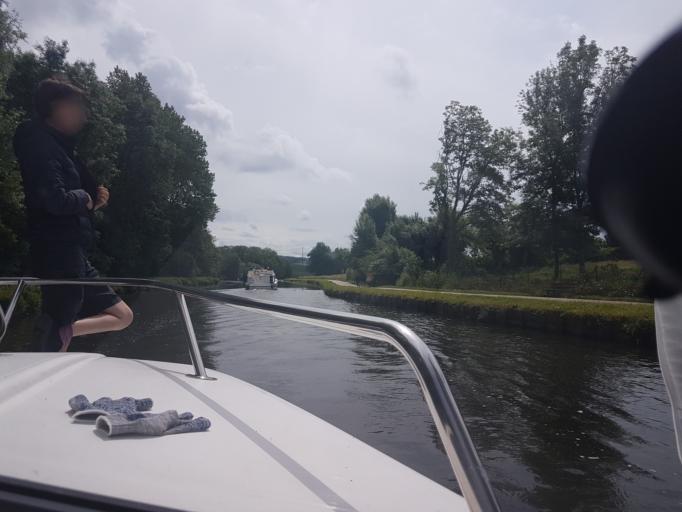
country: FR
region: Bourgogne
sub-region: Departement de l'Yonne
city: Augy
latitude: 47.7836
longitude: 3.5954
